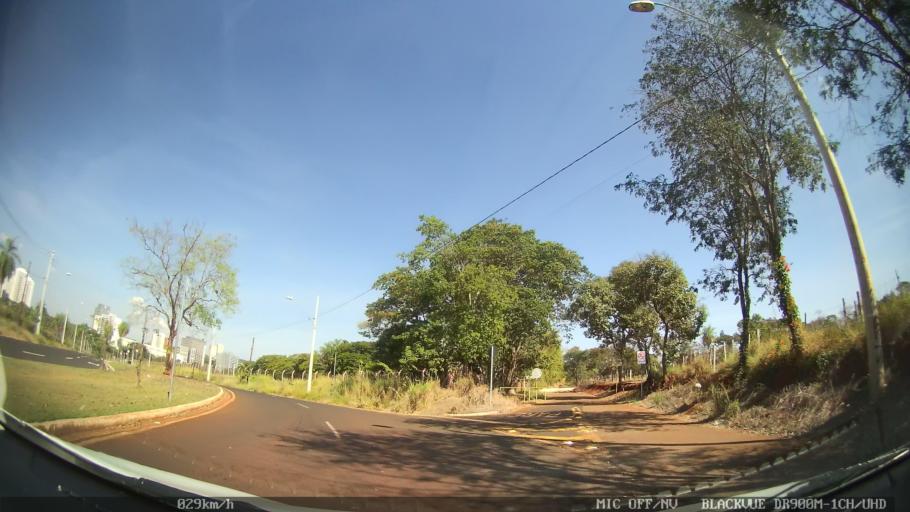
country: BR
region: Sao Paulo
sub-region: Ribeirao Preto
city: Ribeirao Preto
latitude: -21.2174
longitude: -47.8383
